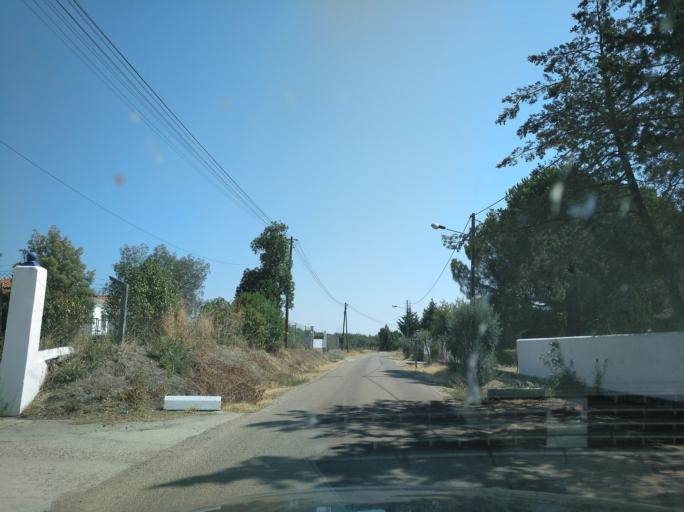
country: PT
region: Portalegre
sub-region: Campo Maior
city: Campo Maior
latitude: 39.0210
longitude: -7.0549
